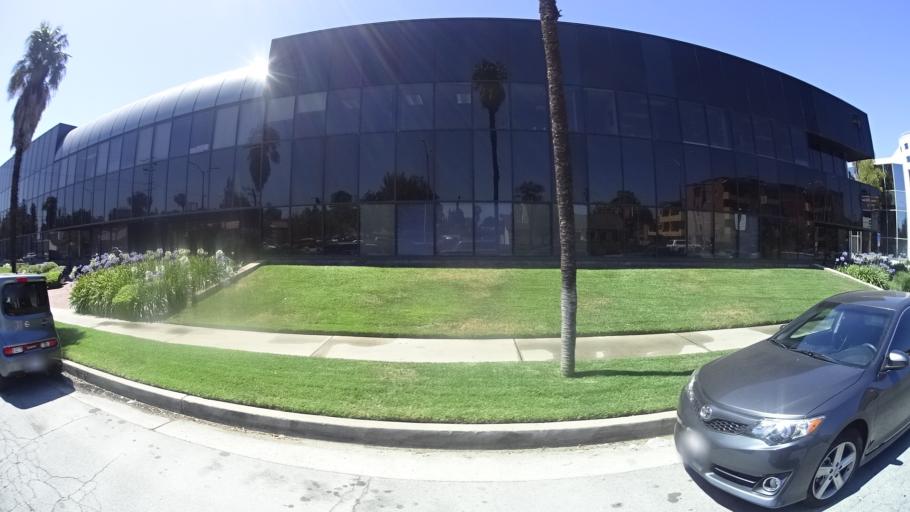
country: US
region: California
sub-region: Los Angeles County
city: Van Nuys
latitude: 34.2011
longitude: -118.4955
